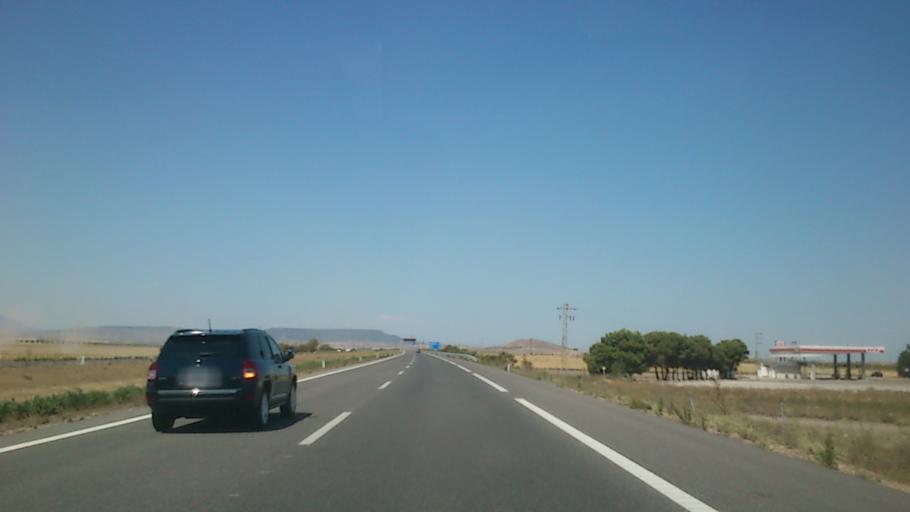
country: ES
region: Aragon
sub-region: Provincia de Zaragoza
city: Gallur
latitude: 41.8444
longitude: -1.3537
